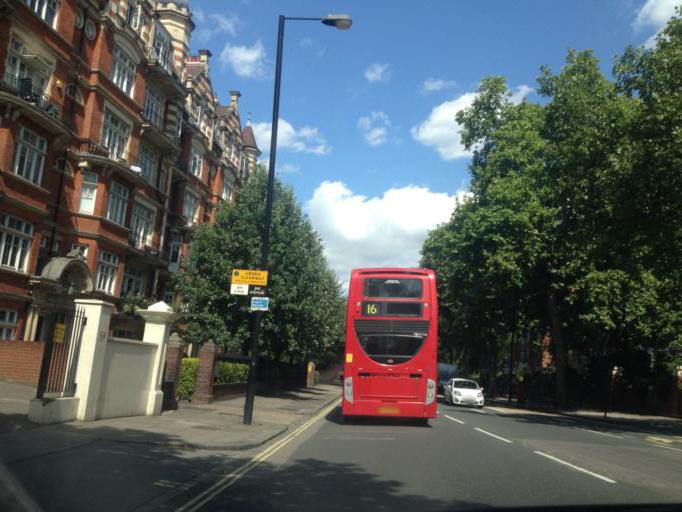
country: GB
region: England
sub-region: Greater London
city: Bayswater
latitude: 51.5262
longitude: -0.1789
